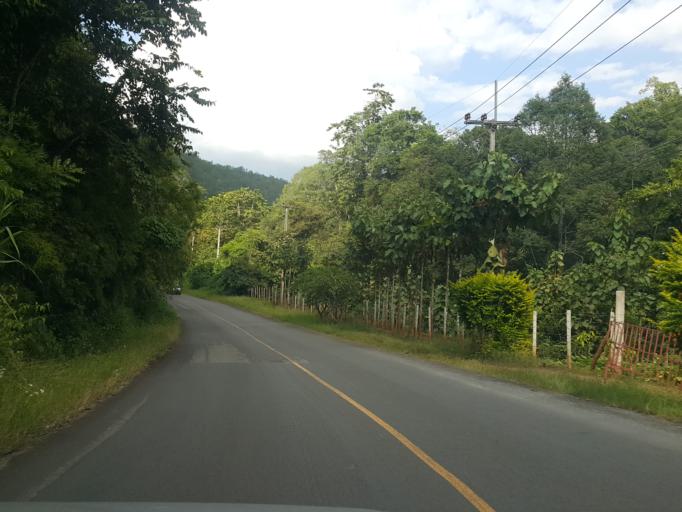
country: TH
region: Chiang Mai
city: Mae Chaem
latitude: 18.5447
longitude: 98.3814
